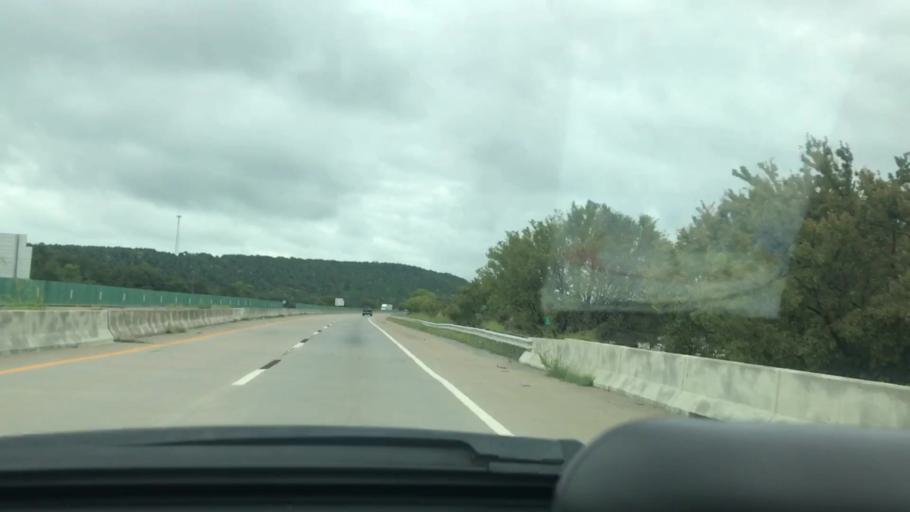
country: US
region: Oklahoma
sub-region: Pittsburg County
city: Krebs
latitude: 35.1067
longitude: -95.6943
